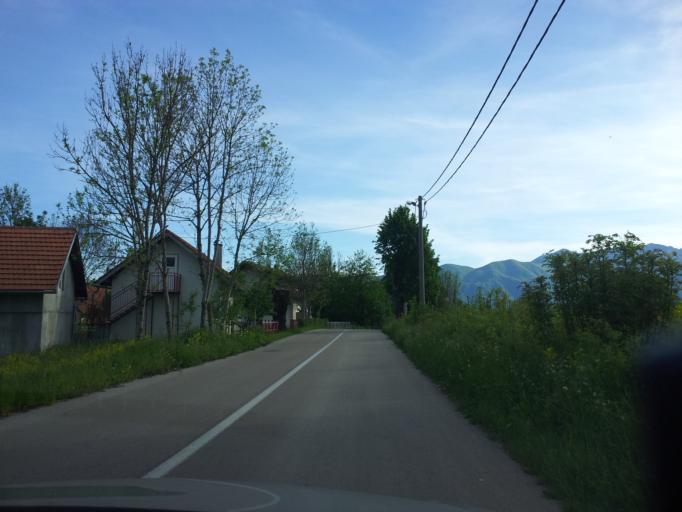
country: HR
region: Zadarska
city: Obrovac
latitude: 44.3815
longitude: 15.6768
